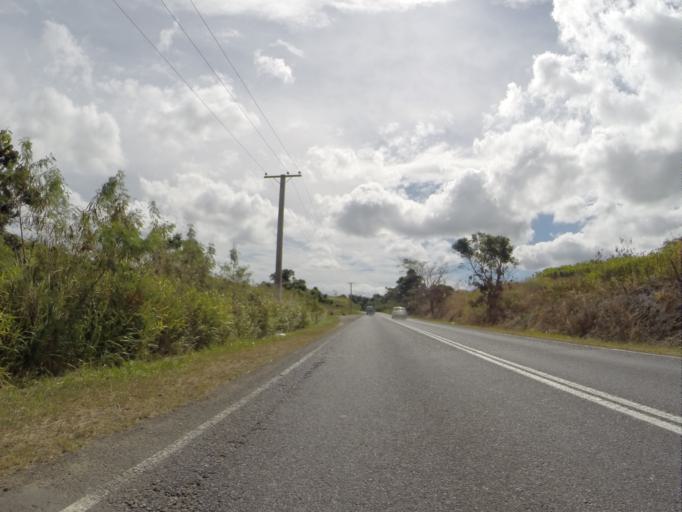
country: FJ
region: Western
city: Nadi
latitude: -18.0988
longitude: 177.3974
